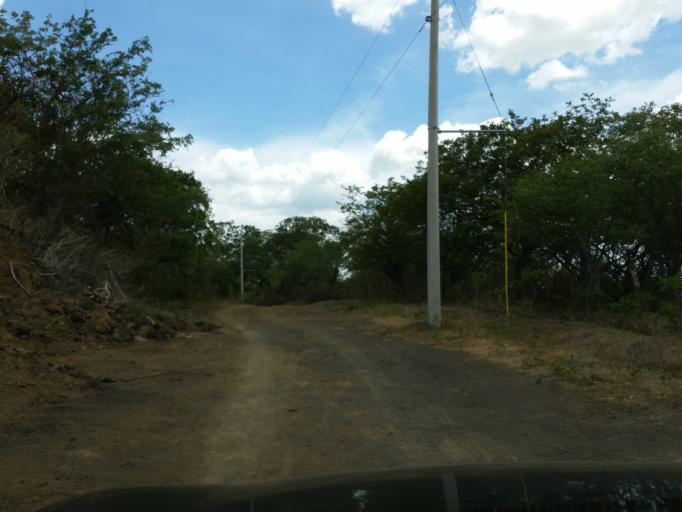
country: NI
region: Managua
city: Carlos Fonseca Amador
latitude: 11.9570
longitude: -86.4376
